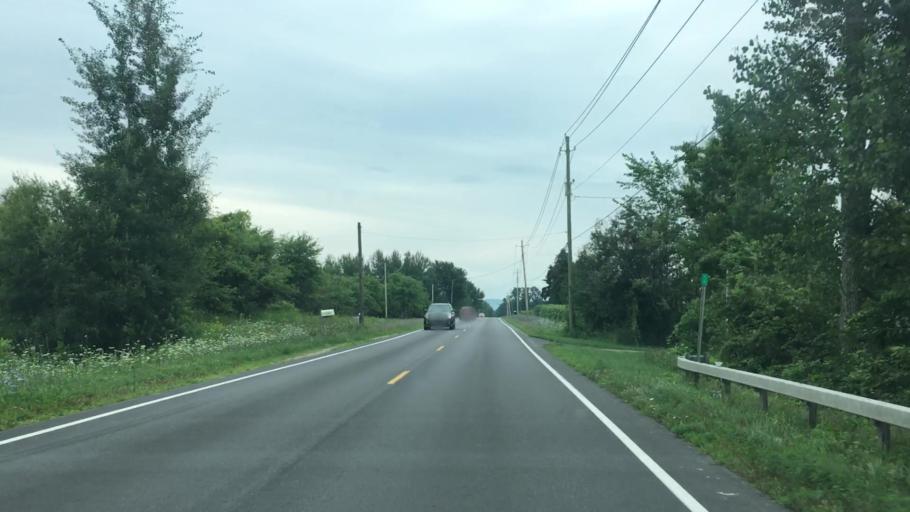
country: US
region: New York
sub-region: Clinton County
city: Peru
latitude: 44.5906
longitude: -73.5721
